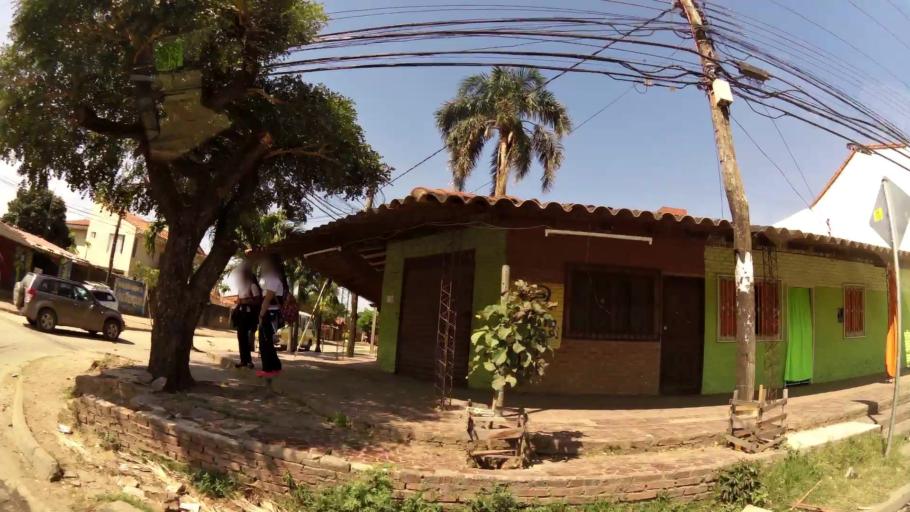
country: BO
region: Santa Cruz
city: Santa Cruz de la Sierra
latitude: -17.7422
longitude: -63.1542
